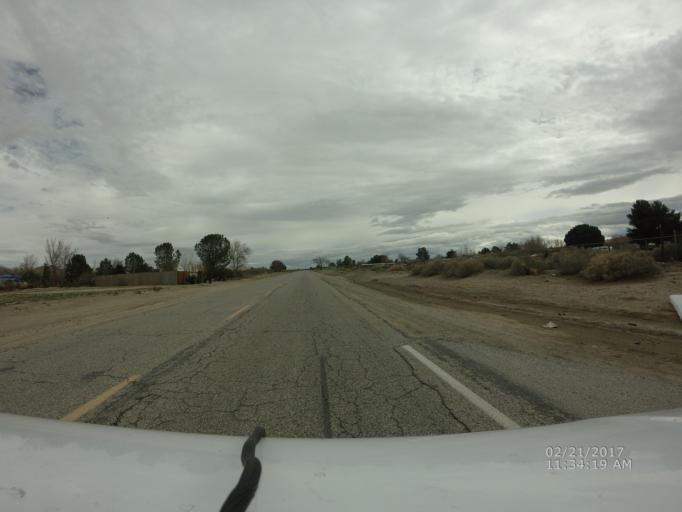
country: US
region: California
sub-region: Los Angeles County
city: Lake Los Angeles
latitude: 34.6311
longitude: -117.8487
